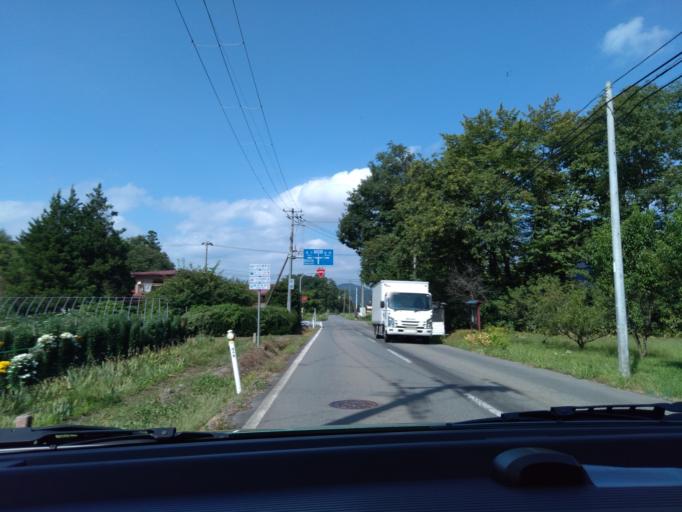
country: JP
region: Iwate
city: Shizukuishi
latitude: 39.6580
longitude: 140.9924
